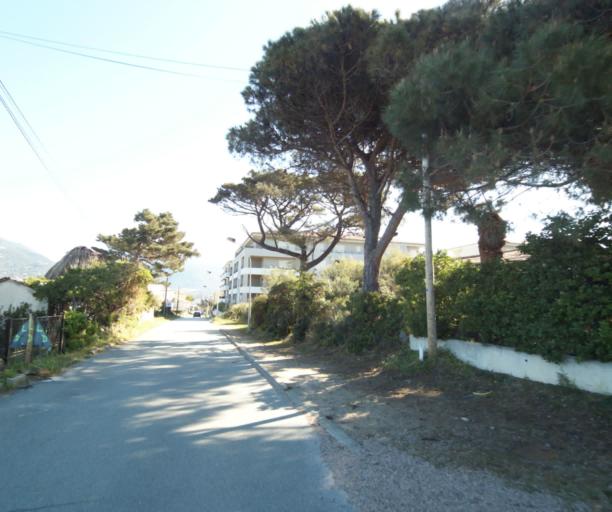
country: FR
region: Corsica
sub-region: Departement de la Corse-du-Sud
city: Propriano
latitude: 41.6735
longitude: 8.8970
